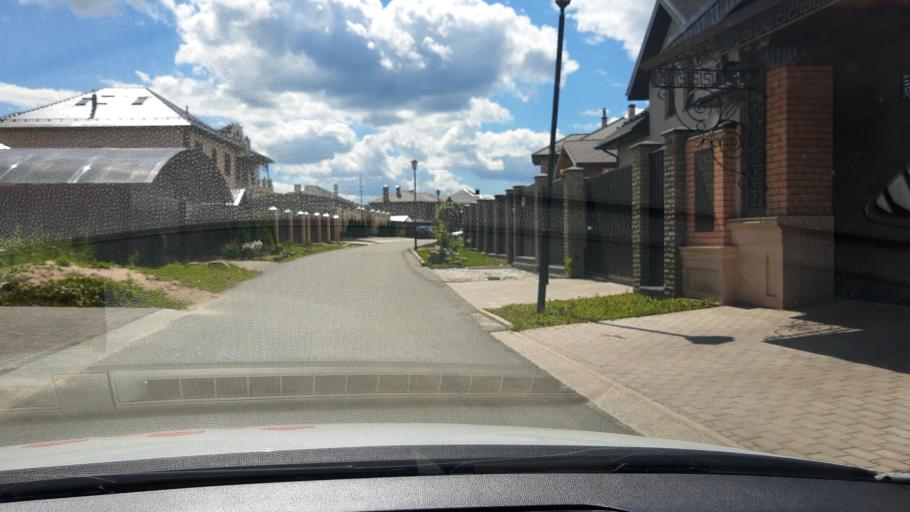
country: RU
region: Moskovskaya
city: Poselok Mar'ino
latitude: 55.5445
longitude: 37.3362
